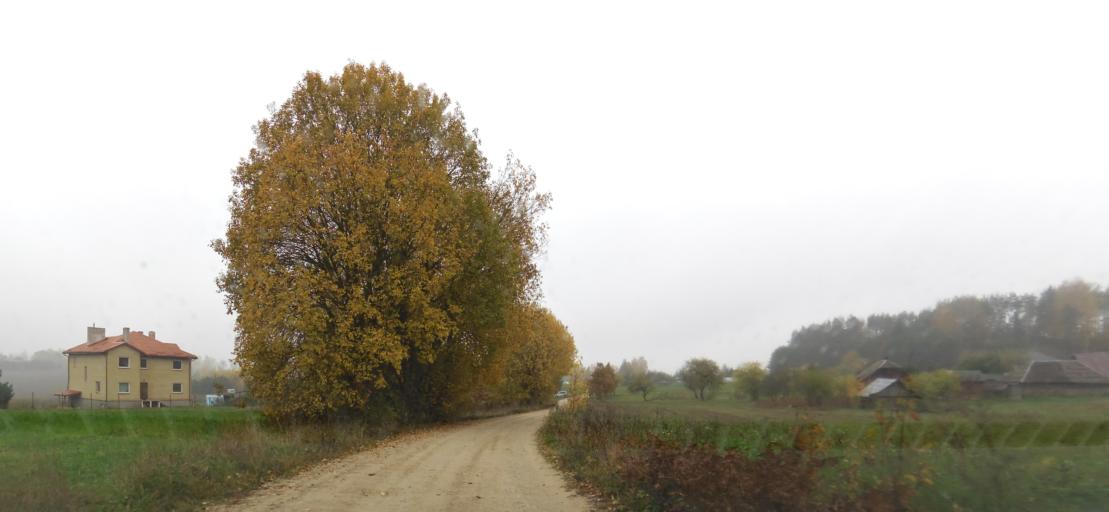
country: LT
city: Skaidiskes
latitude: 54.6225
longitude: 25.4724
